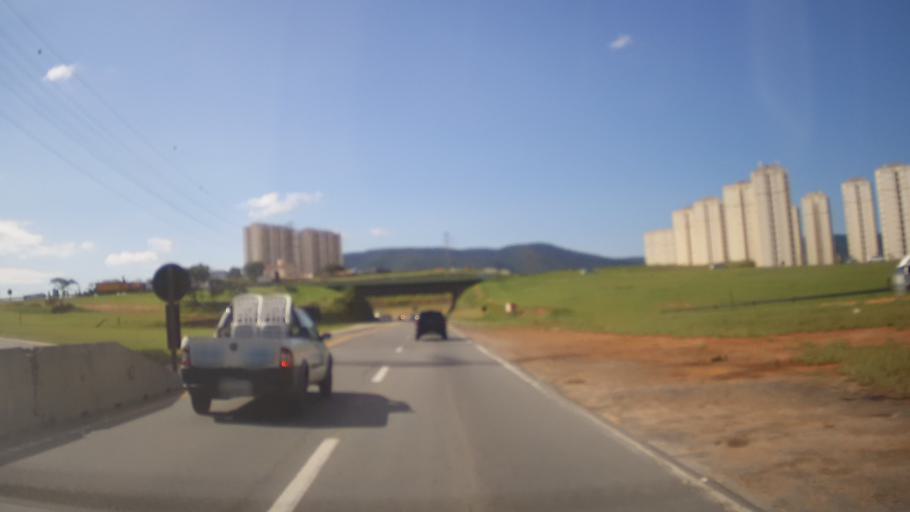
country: BR
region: Sao Paulo
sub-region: Jundiai
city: Jundiai
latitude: -23.1820
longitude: -46.9709
